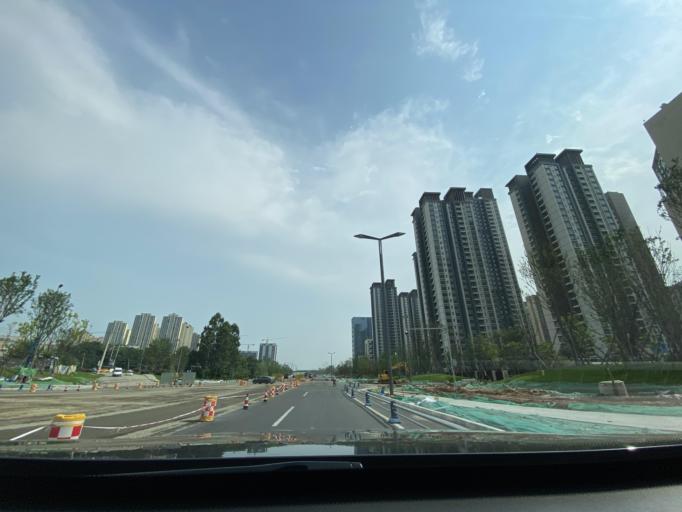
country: CN
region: Sichuan
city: Longquan
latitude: 30.4209
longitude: 104.1015
